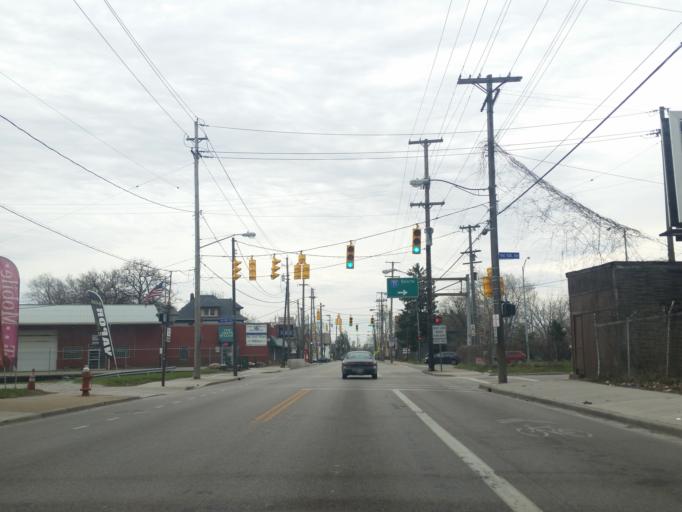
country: US
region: Ohio
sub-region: Cuyahoga County
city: Brooklyn
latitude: 41.4578
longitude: -81.7283
